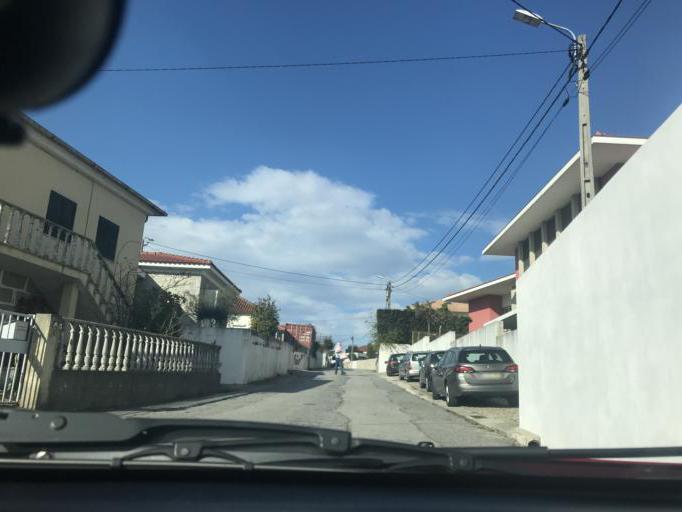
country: PT
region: Braga
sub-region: Vila Nova de Famalicao
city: Vila Nova de Famalicao
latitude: 41.4160
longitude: -8.5092
